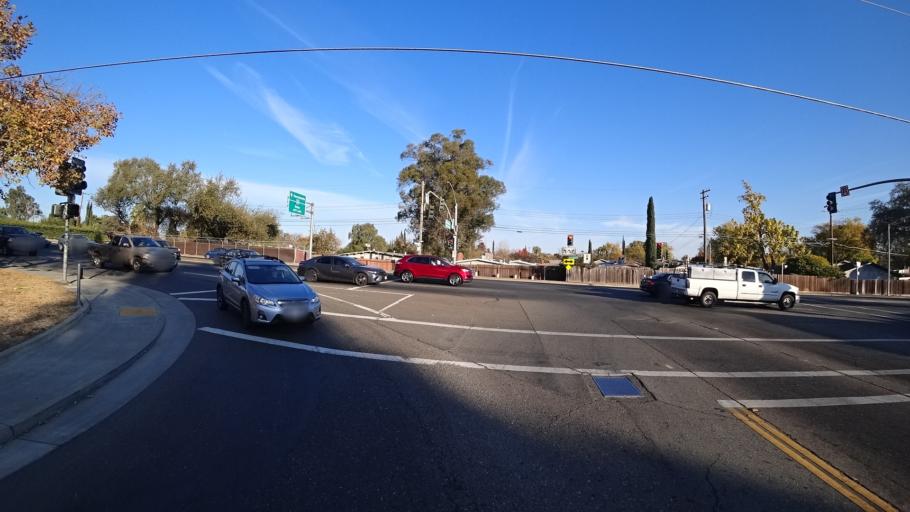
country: US
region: California
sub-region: Sacramento County
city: Antelope
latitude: 38.7073
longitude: -121.3058
